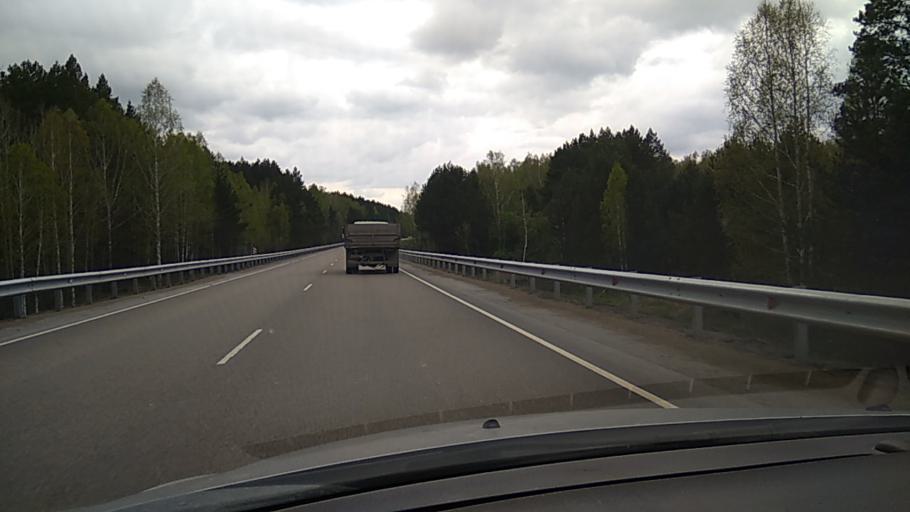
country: RU
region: Kurgan
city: Kataysk
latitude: 56.2980
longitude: 62.3845
